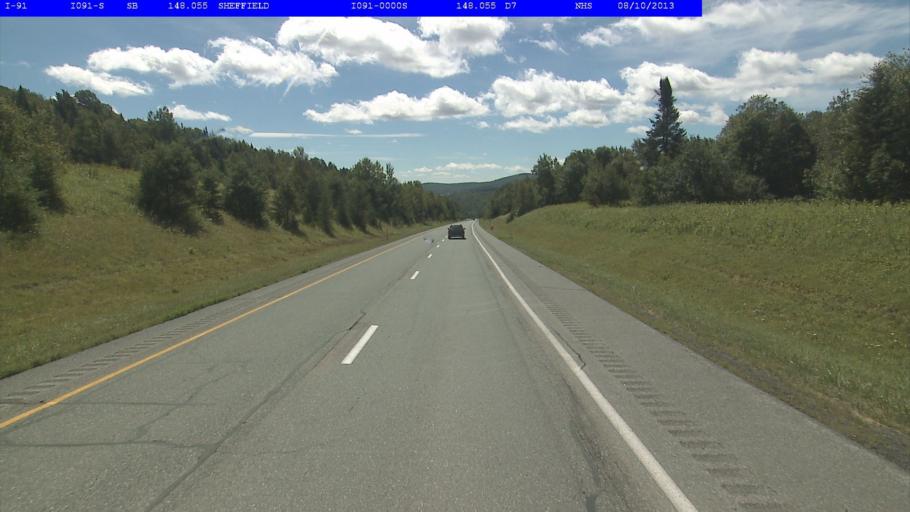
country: US
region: Vermont
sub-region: Caledonia County
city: Lyndonville
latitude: 44.6366
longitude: -72.1308
